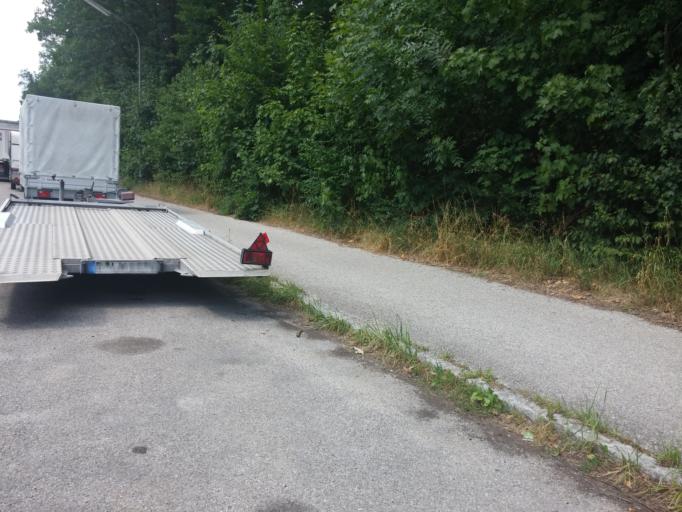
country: DE
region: Bavaria
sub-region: Upper Bavaria
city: Unterhaching
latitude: 48.0844
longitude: 11.6011
